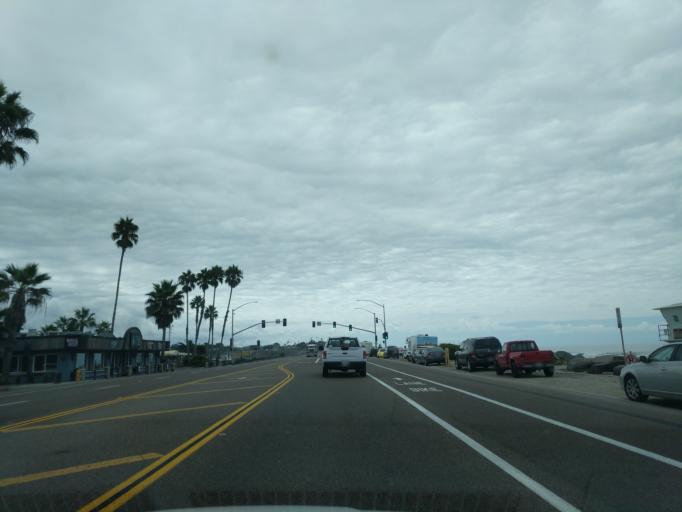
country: US
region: California
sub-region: San Diego County
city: Solana Beach
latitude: 33.0119
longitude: -117.2795
